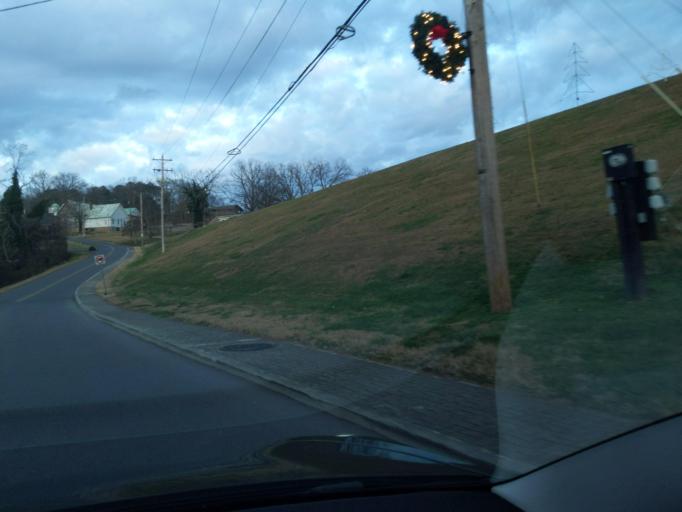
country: US
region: Tennessee
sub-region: Jefferson County
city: Dandridge
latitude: 36.0157
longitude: -83.4134
